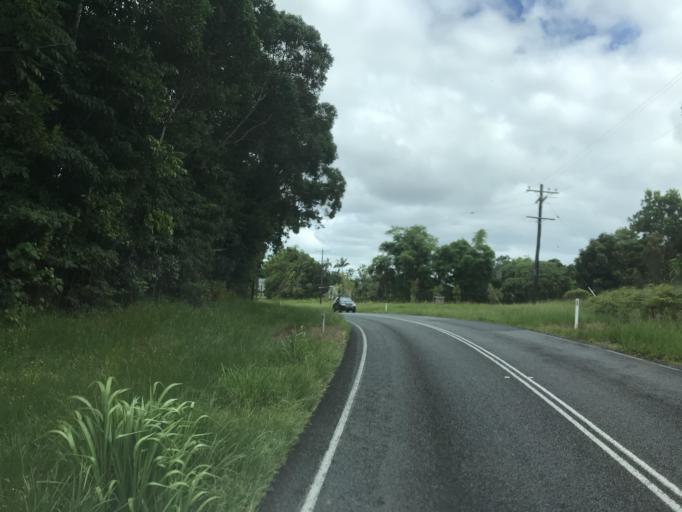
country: AU
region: Queensland
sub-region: Cassowary Coast
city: Innisfail
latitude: -17.8290
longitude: 146.0557
